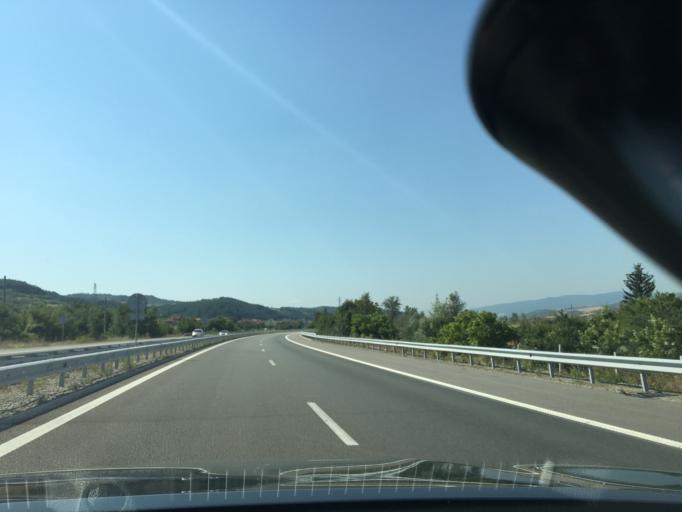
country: BG
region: Kyustendil
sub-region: Obshtina Dupnitsa
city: Dupnitsa
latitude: 42.2341
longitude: 23.0836
